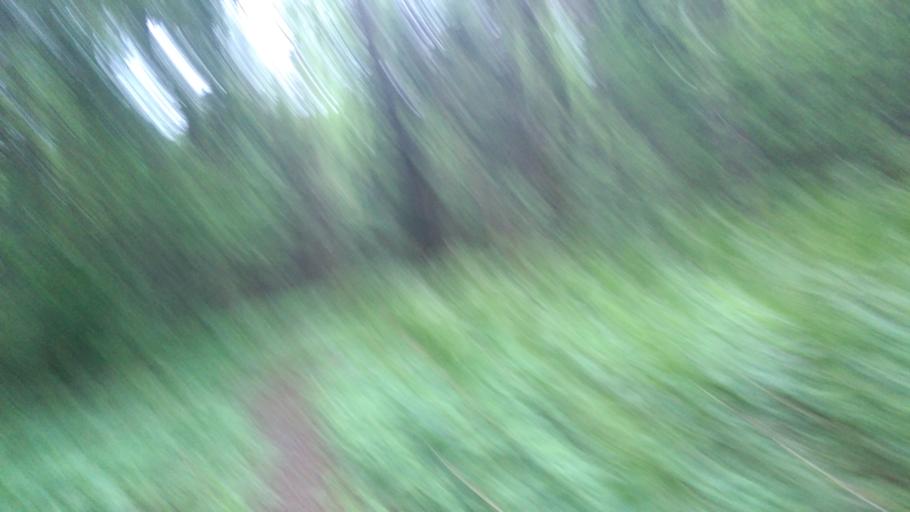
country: RU
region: Perm
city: Froly
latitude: 57.9603
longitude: 56.3100
